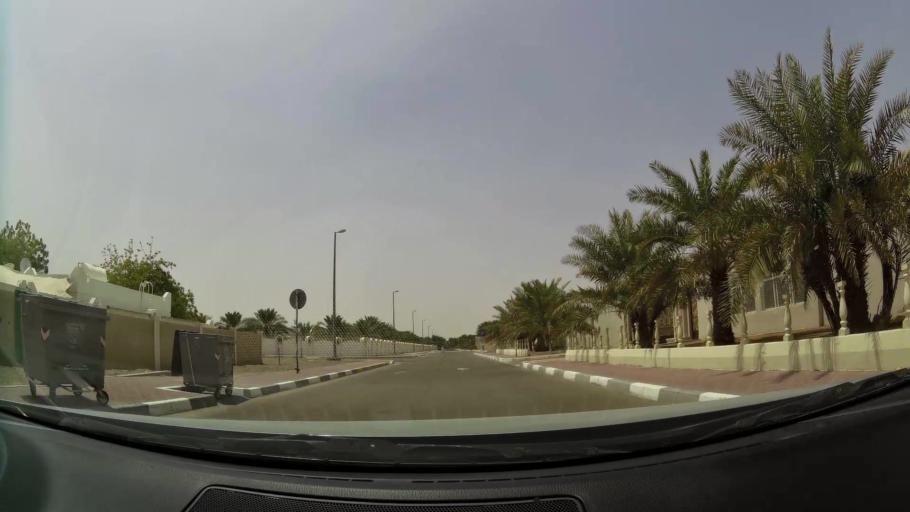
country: AE
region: Abu Dhabi
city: Al Ain
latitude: 24.1861
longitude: 55.6755
